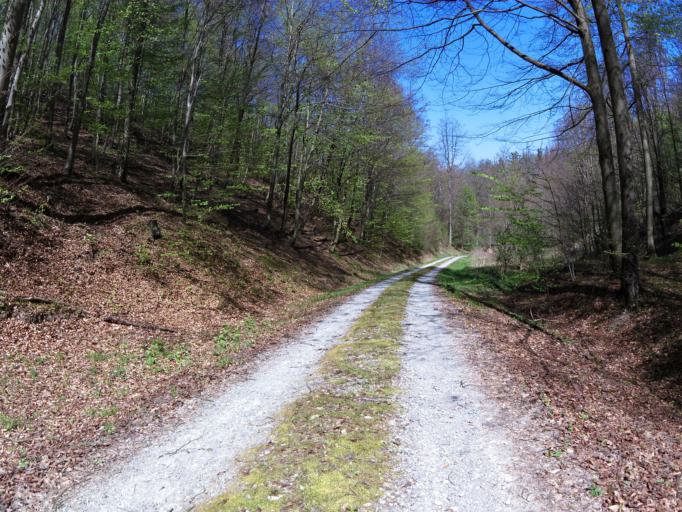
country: DE
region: Thuringia
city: Krauthausen
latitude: 50.9794
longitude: 10.2417
